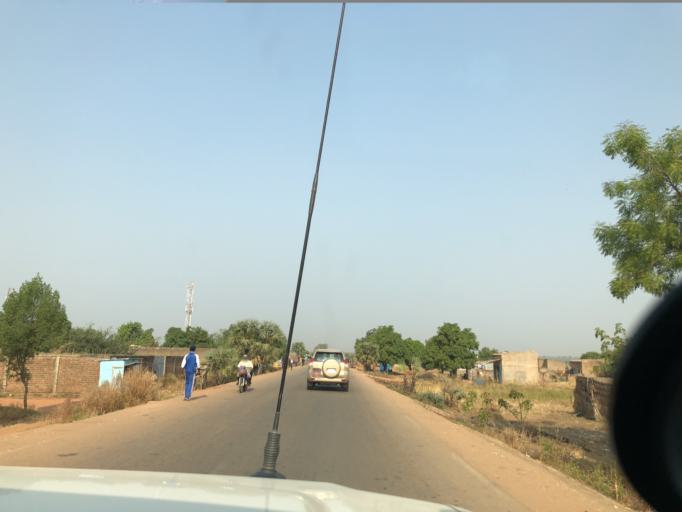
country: TD
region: Logone Occidental
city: Moundou
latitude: 8.5712
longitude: 16.0455
